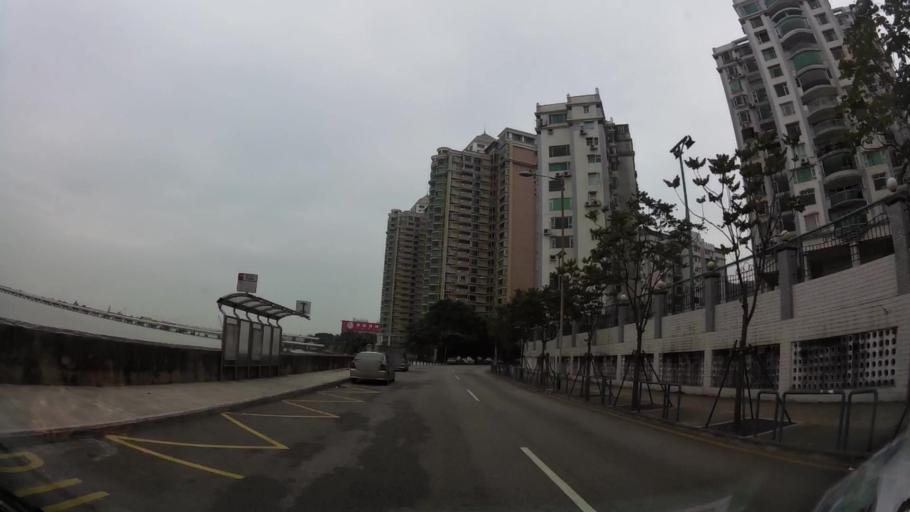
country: MO
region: Macau
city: Macau
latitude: 22.1654
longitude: 113.5600
